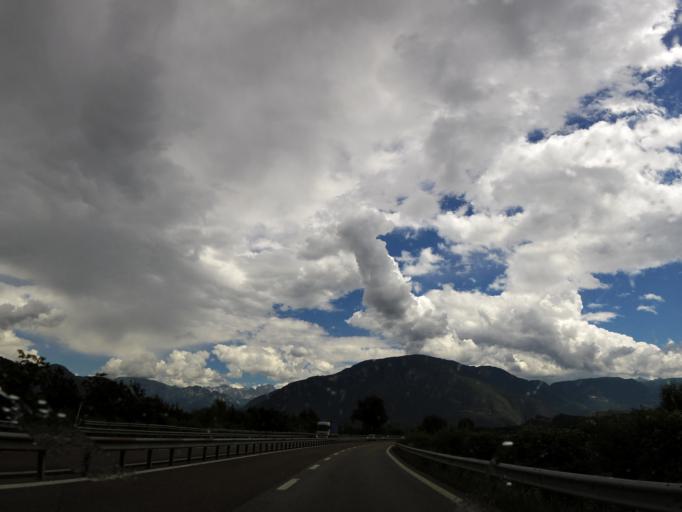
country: IT
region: Trentino-Alto Adige
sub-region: Bolzano
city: San Paolo
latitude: 46.4973
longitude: 11.2766
